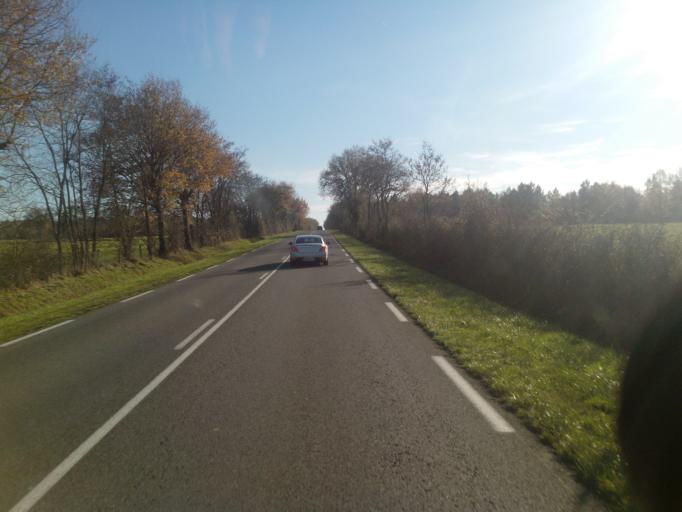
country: FR
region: Poitou-Charentes
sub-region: Departement de la Vienne
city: Lussac-les-Chateaux
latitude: 46.3612
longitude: 0.7750
